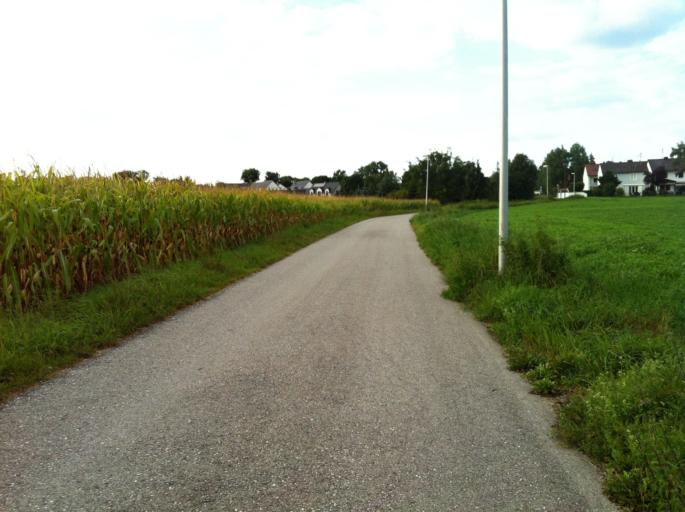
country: DE
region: Bavaria
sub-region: Upper Bavaria
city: Garching bei Munchen
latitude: 48.2764
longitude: 11.6778
